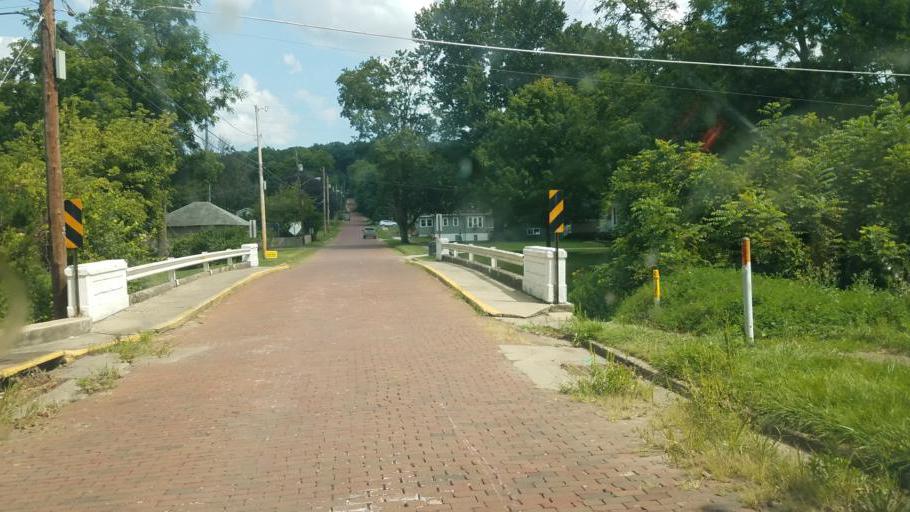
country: US
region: Ohio
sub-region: Knox County
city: Mount Vernon
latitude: 40.3918
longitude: -82.4688
